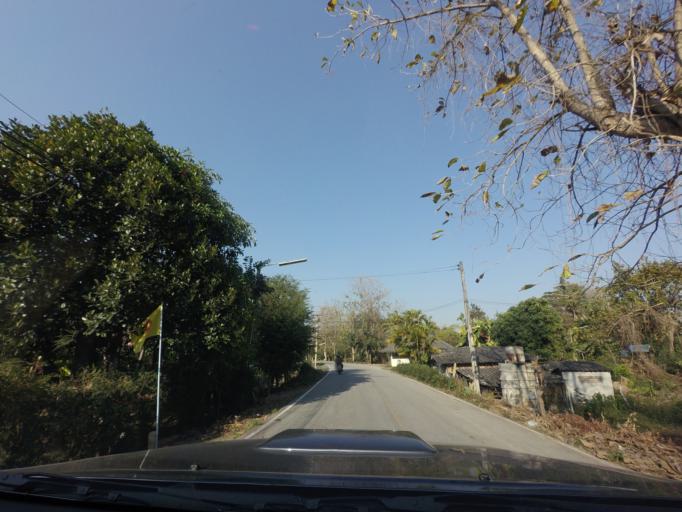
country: TH
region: Chiang Mai
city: San Sai
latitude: 18.9268
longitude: 98.9653
